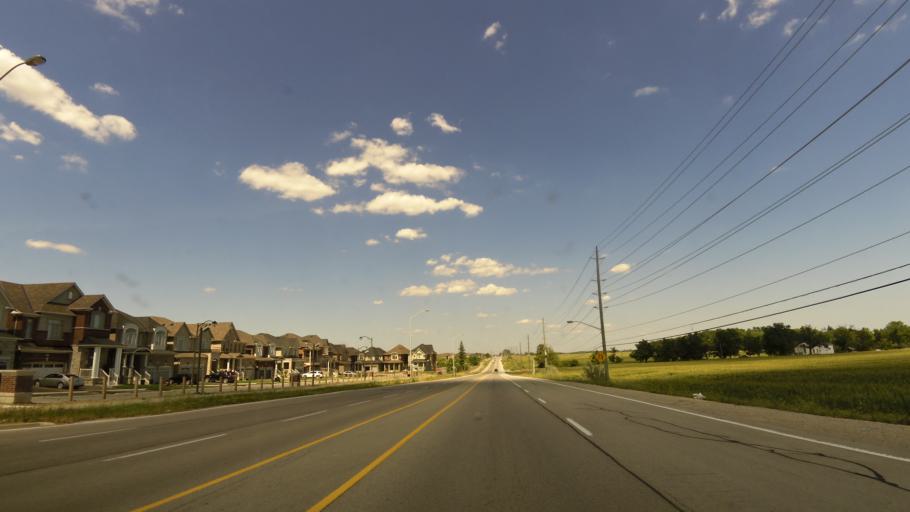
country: CA
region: Ontario
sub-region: Halton
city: Milton
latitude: 43.6185
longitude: -79.8833
